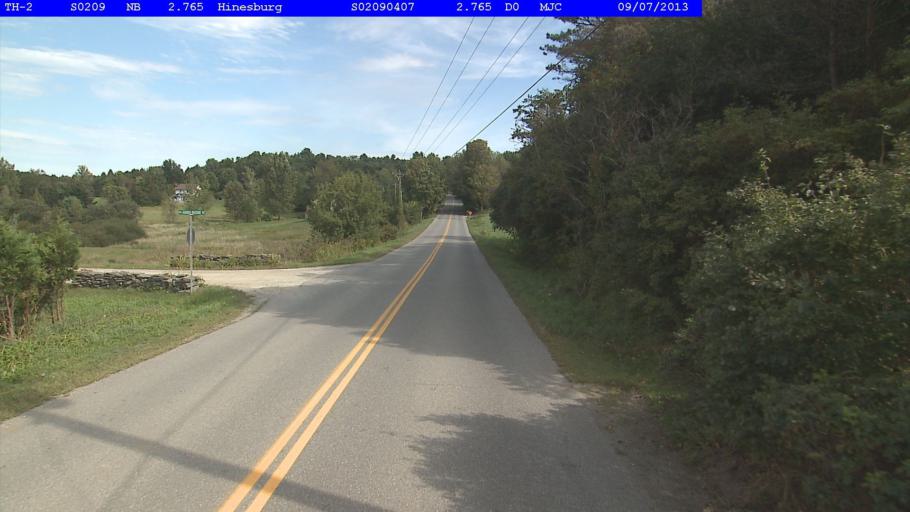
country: US
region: Vermont
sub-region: Chittenden County
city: Hinesburg
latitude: 44.3510
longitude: -73.0762
